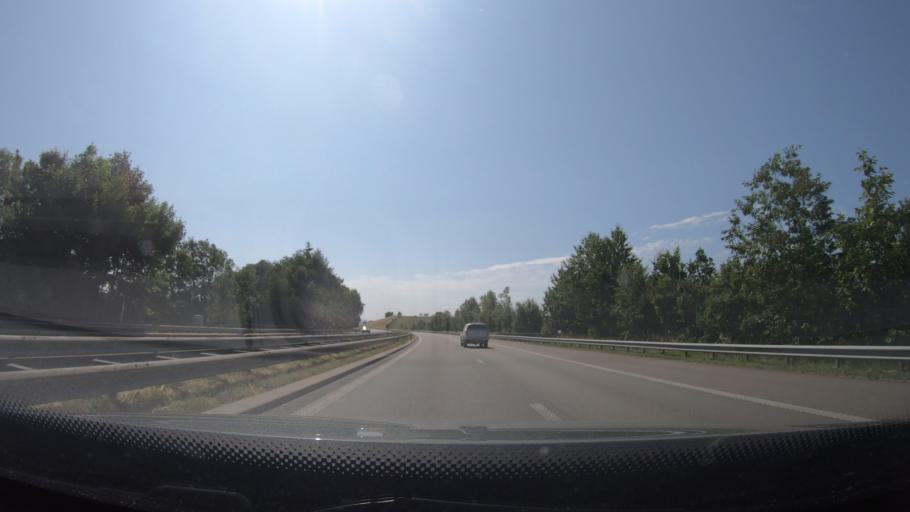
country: BE
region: Wallonia
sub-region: Province de Liege
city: Saint-Vith
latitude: 50.2970
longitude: 6.0829
